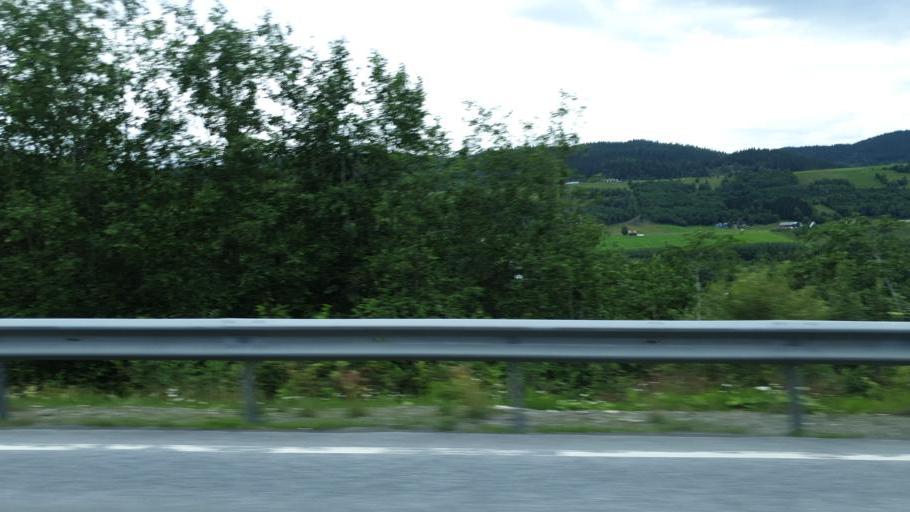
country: NO
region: Sor-Trondelag
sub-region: Melhus
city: Lundamo
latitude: 63.1134
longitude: 10.2400
